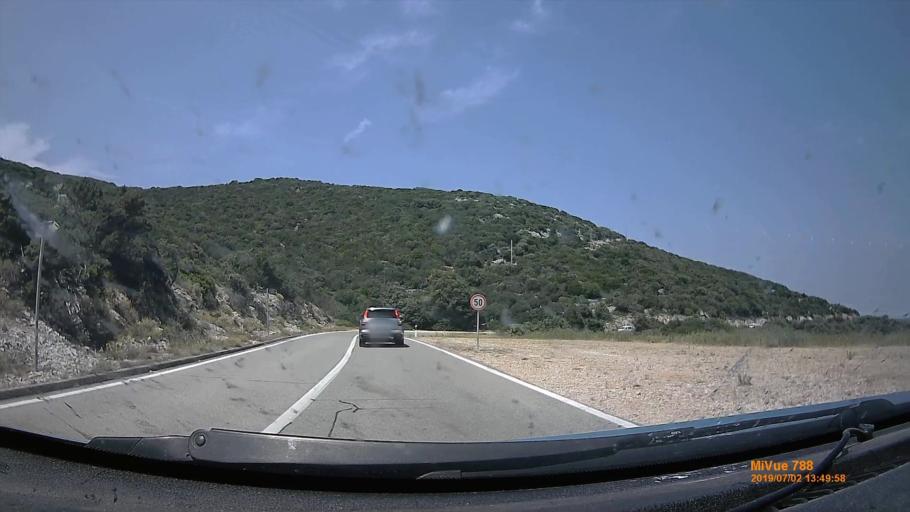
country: HR
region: Primorsko-Goranska
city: Mali Losinj
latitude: 44.5931
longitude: 14.4074
